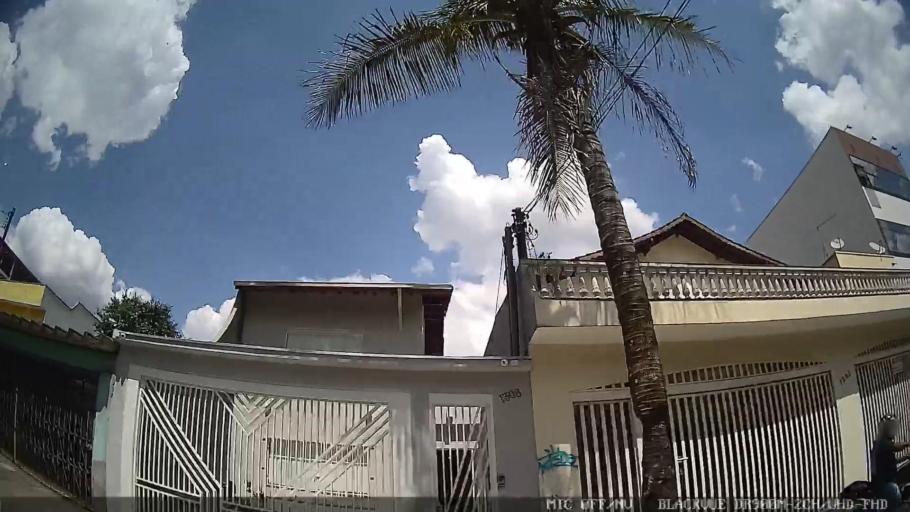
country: BR
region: Sao Paulo
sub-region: Ferraz De Vasconcelos
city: Ferraz de Vasconcelos
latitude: -23.5440
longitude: -46.4522
